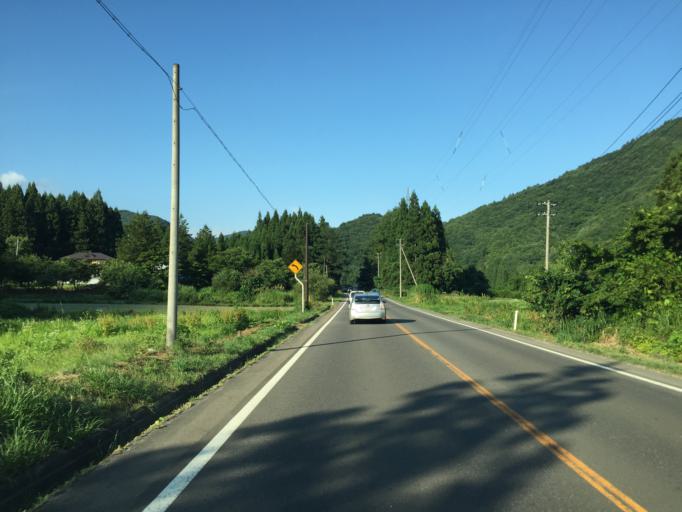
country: JP
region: Fukushima
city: Inawashiro
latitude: 37.6136
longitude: 140.1424
